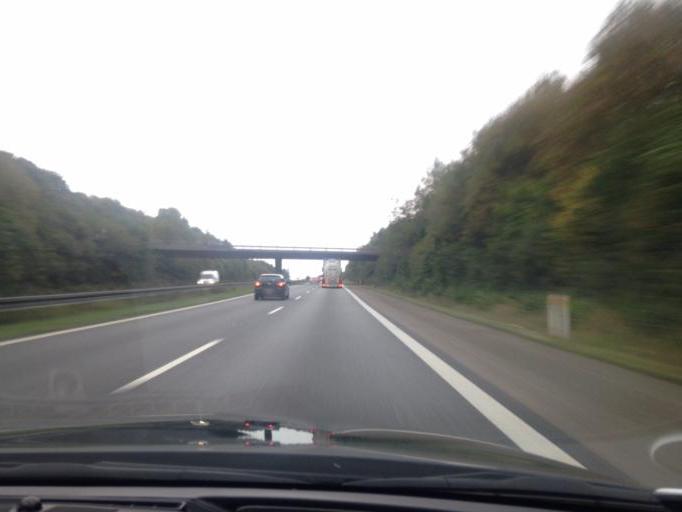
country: DK
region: South Denmark
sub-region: Kolding Kommune
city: Christiansfeld
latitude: 55.3592
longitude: 9.4485
